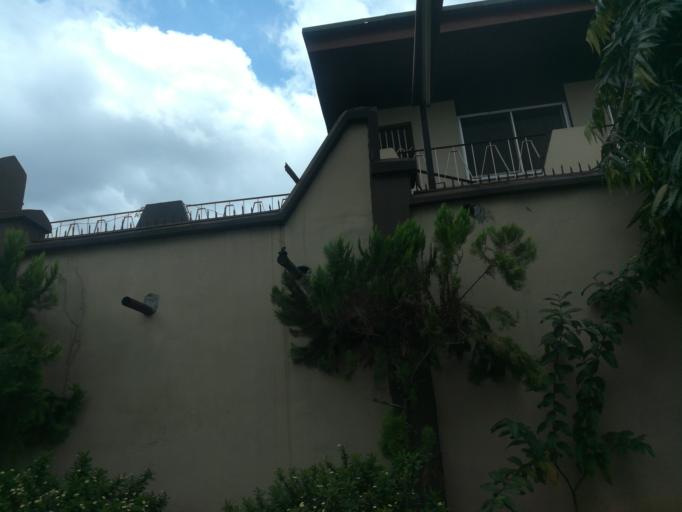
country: NG
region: Lagos
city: Somolu
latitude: 6.5546
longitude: 3.3637
